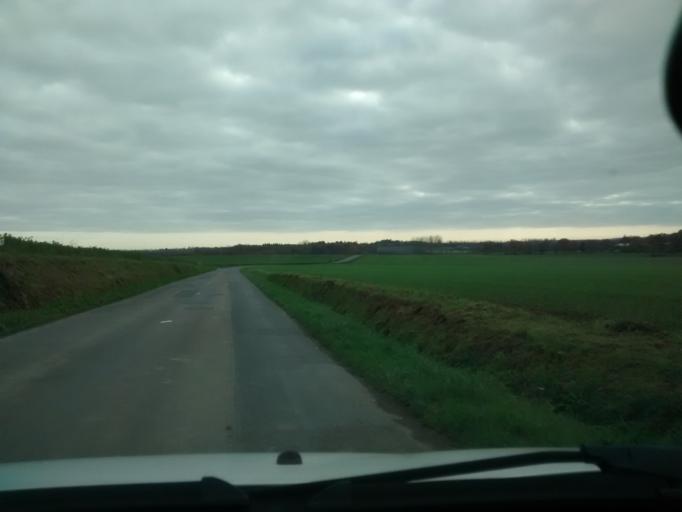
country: FR
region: Brittany
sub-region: Departement d'Ille-et-Vilaine
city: Chavagne
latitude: 48.0784
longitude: -1.7711
